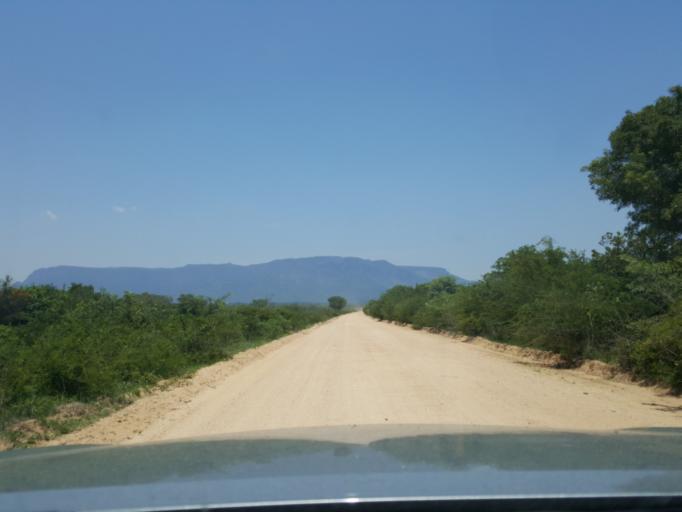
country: ZA
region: Limpopo
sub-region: Mopani District Municipality
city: Hoedspruit
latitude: -24.5652
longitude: 31.0116
